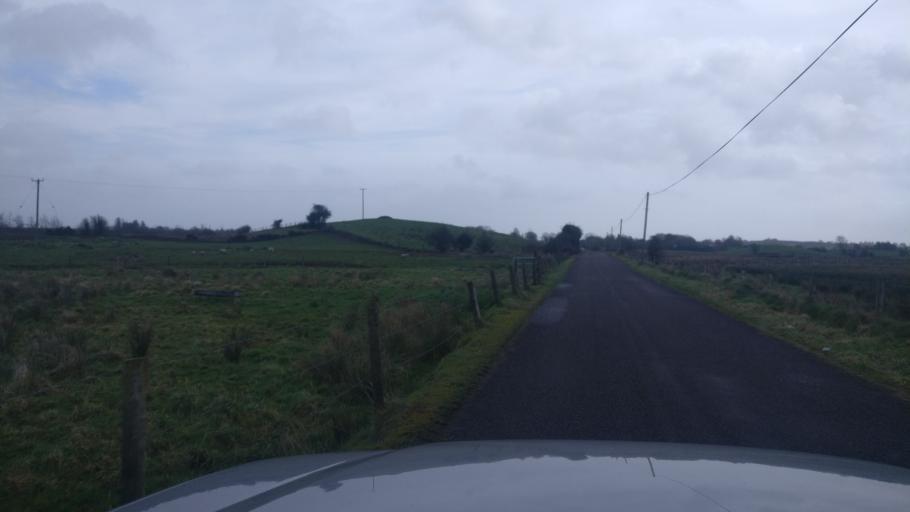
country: IE
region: Connaught
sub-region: County Galway
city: Loughrea
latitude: 53.2824
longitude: -8.4560
